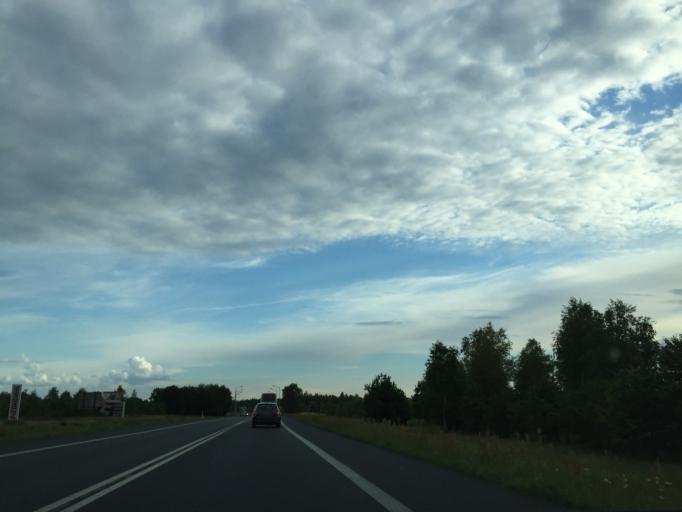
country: PL
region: Lublin Voivodeship
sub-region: Powiat lubartowski
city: Lubartow
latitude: 51.4674
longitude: 22.5800
